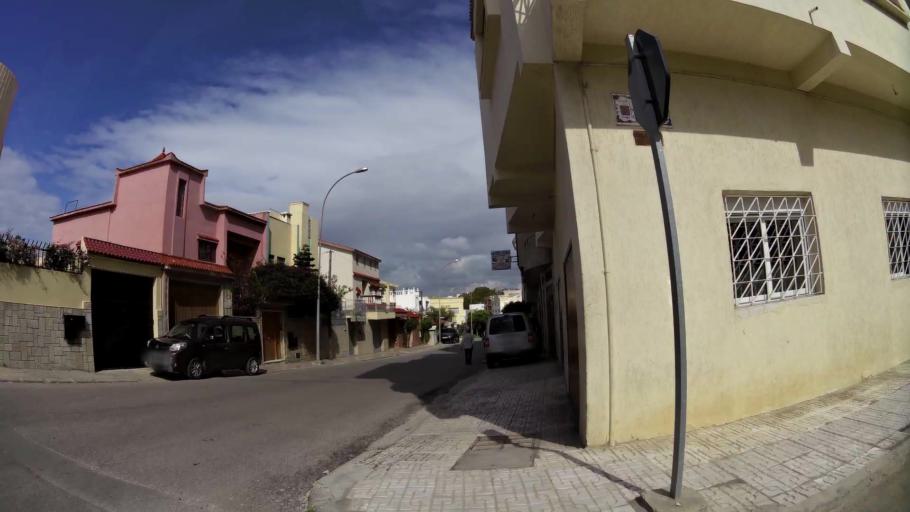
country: MA
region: Tanger-Tetouan
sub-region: Tanger-Assilah
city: Tangier
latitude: 35.7641
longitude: -5.8063
